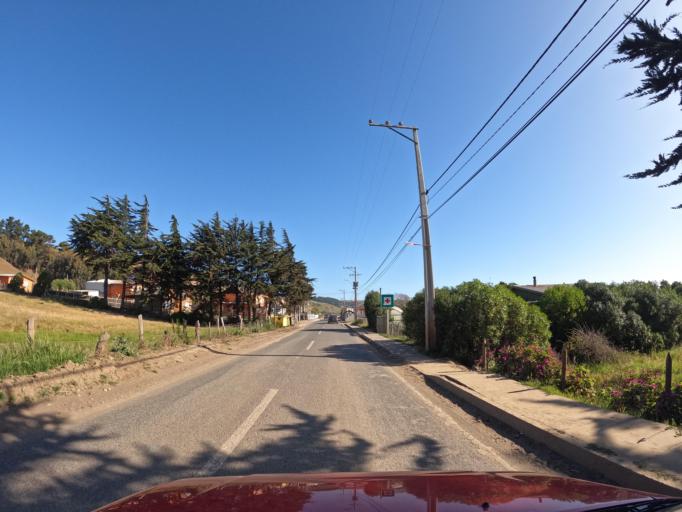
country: CL
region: Maule
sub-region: Provincia de Talca
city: Constitucion
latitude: -34.8489
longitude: -72.1414
